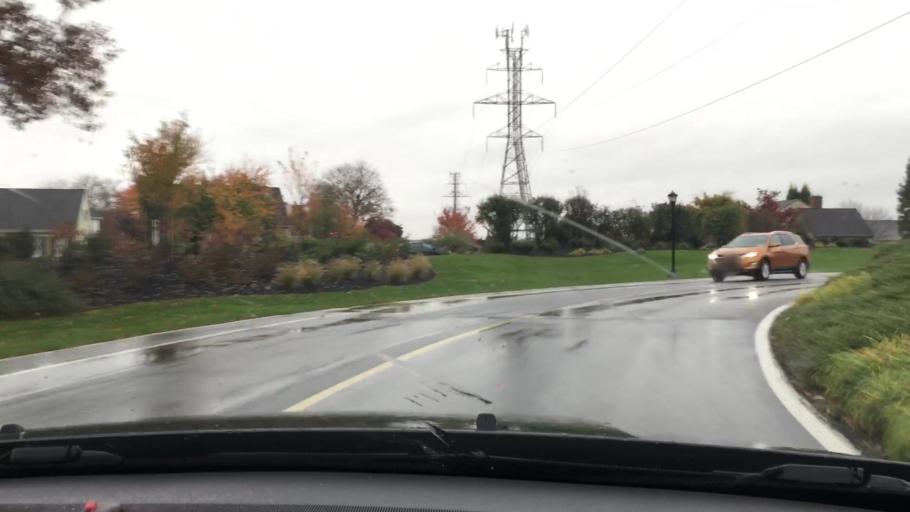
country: US
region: Pennsylvania
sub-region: Lancaster County
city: Willow Street
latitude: 39.9950
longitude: -76.2823
